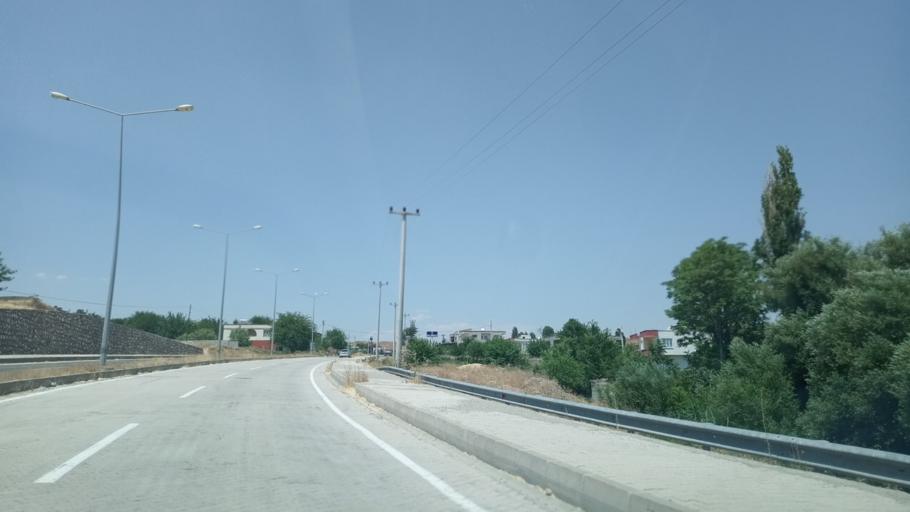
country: TR
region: Batman
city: Bekirhan
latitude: 38.1417
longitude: 41.2916
